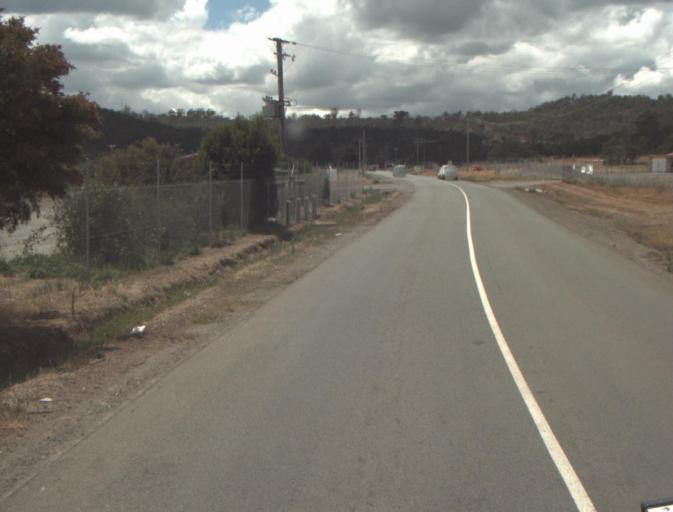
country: AU
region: Tasmania
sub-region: Launceston
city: Newnham
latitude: -41.4017
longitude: 147.1475
